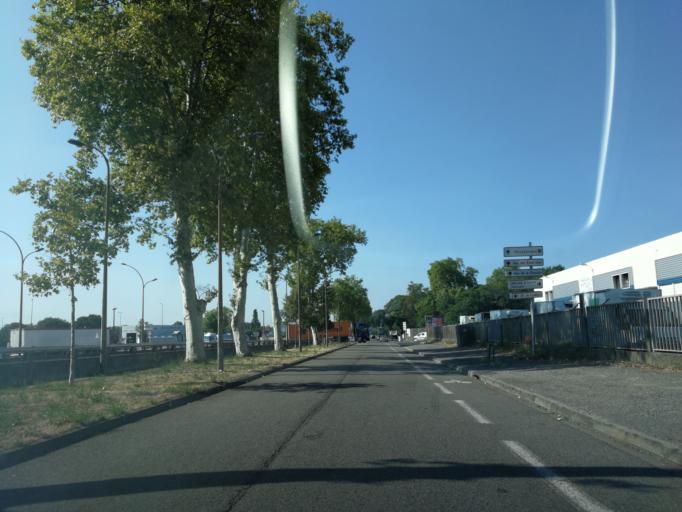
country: FR
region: Midi-Pyrenees
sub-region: Departement de la Haute-Garonne
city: Aucamville
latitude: 43.6416
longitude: 1.4288
